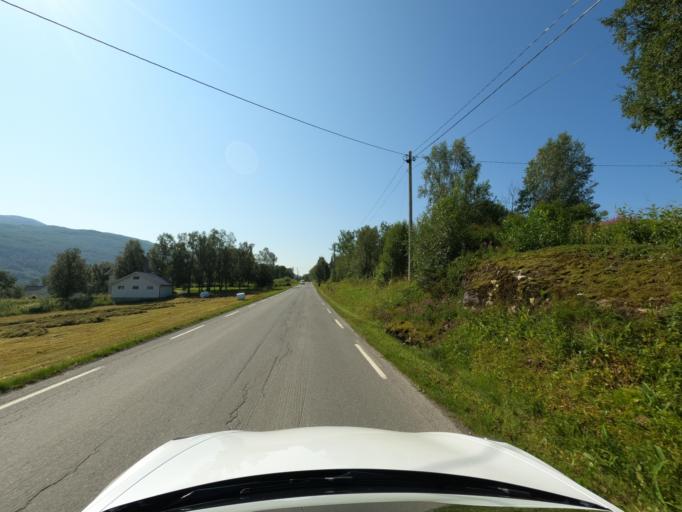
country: NO
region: Nordland
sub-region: Ballangen
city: Ballangen
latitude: 68.3544
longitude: 16.8651
